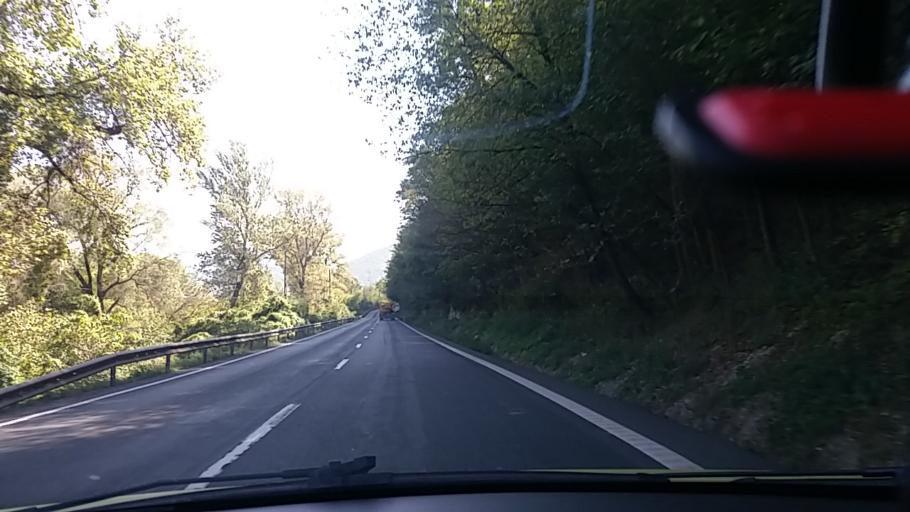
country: RO
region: Hunedoara
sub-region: Comuna Branisca
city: Branisca
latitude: 45.9093
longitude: 22.7715
